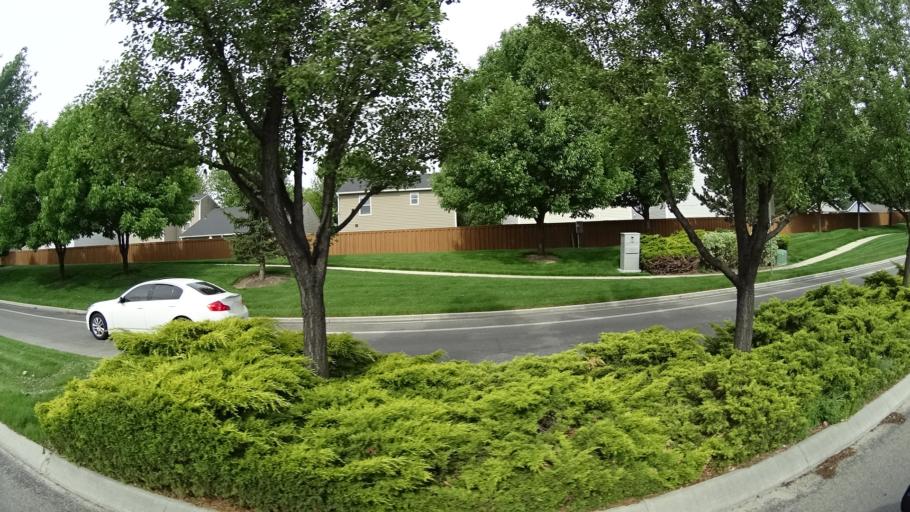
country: US
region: Idaho
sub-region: Ada County
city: Garden City
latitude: 43.5448
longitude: -116.2990
